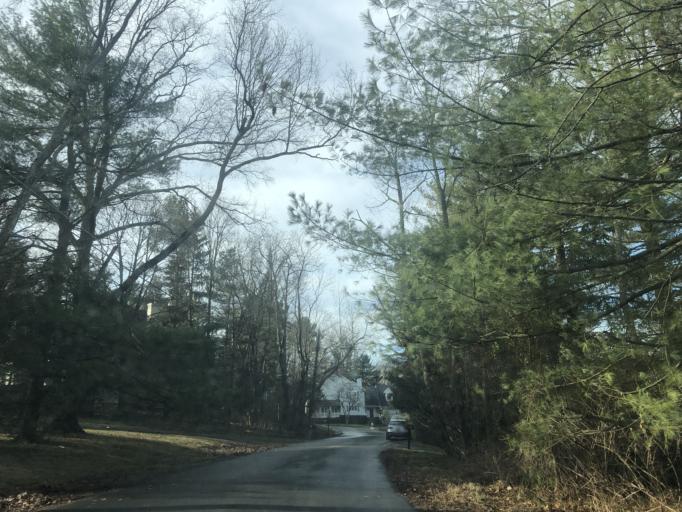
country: US
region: New Jersey
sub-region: Somerset County
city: Kingston
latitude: 40.3624
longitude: -74.6328
